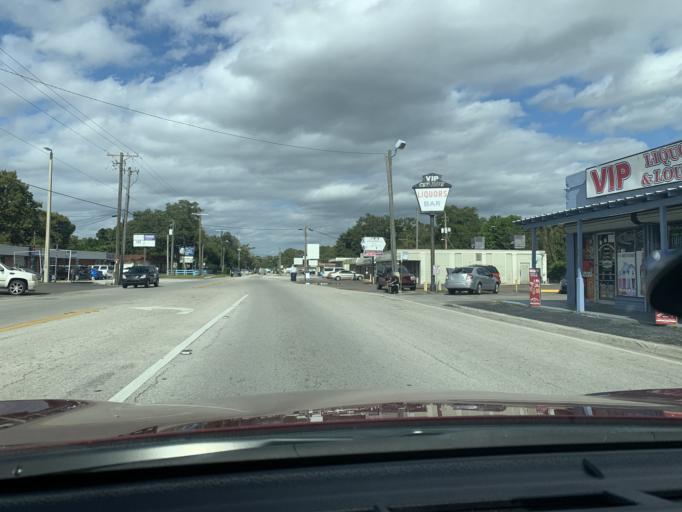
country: US
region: Florida
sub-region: Hillsborough County
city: Egypt Lake-Leto
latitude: 28.0117
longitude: -82.4845
